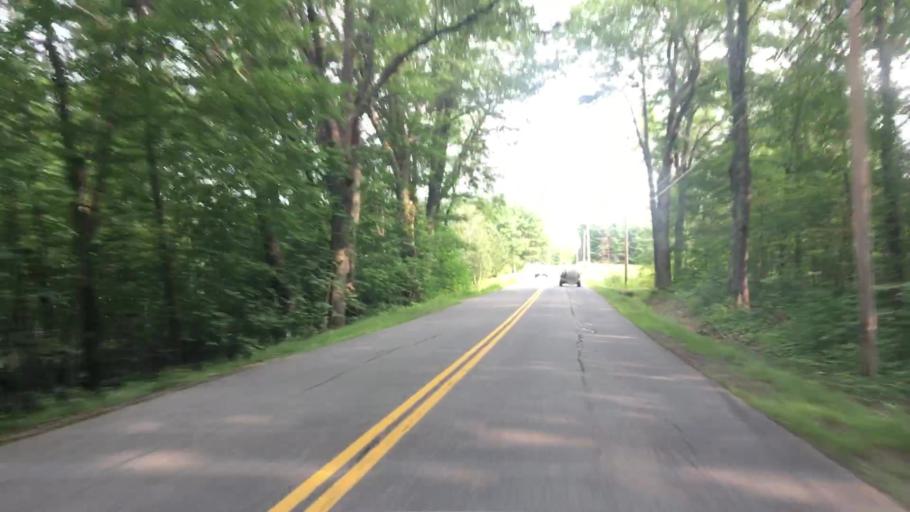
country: US
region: Maine
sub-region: Kennebec County
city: Chelsea
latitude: 44.2979
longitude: -69.6970
